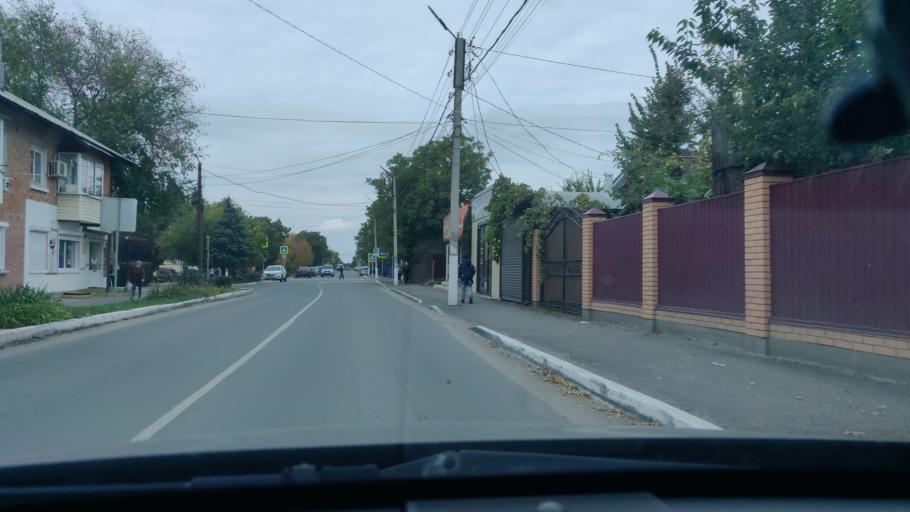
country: RU
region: Rostov
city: Ust'-Donetskiy
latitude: 47.6417
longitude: 40.8690
